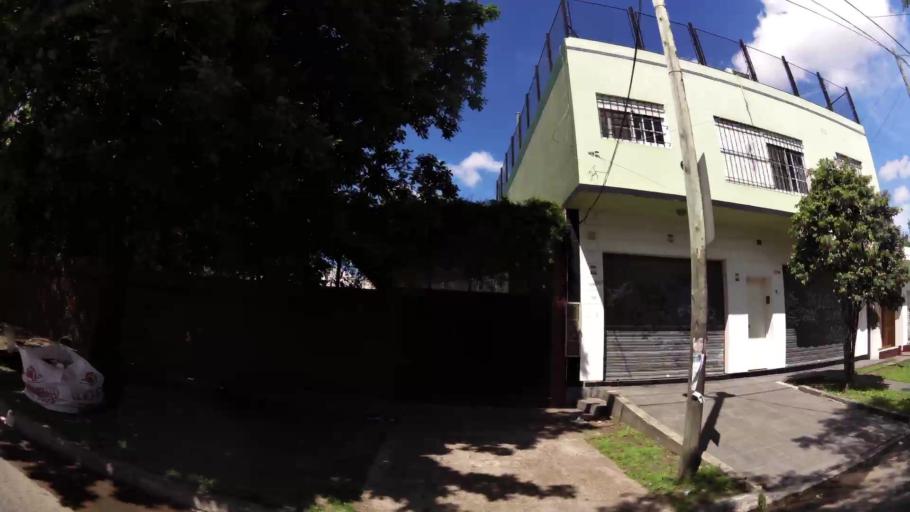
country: AR
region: Buenos Aires
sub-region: Partido de Quilmes
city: Quilmes
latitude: -34.8141
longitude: -58.2725
